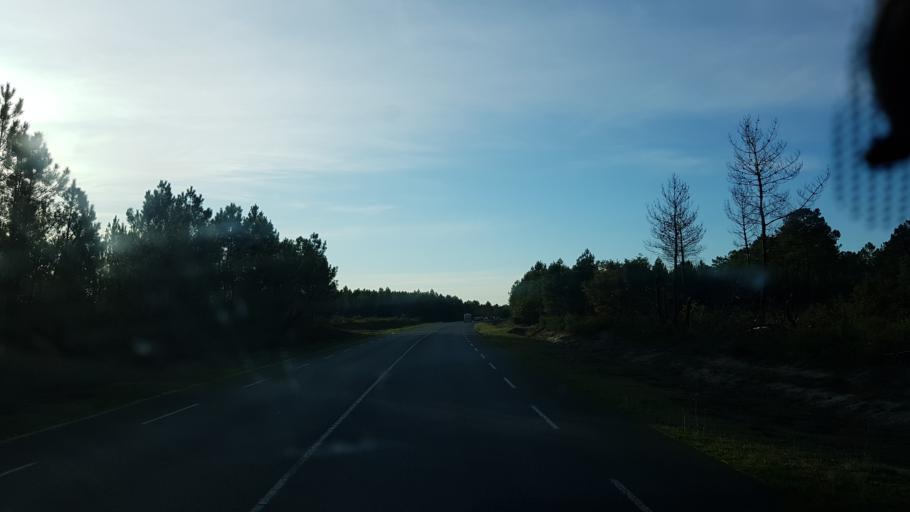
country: FR
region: Aquitaine
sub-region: Departement de la Gironde
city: Martignas-sur-Jalle
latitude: 44.8300
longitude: -0.7868
